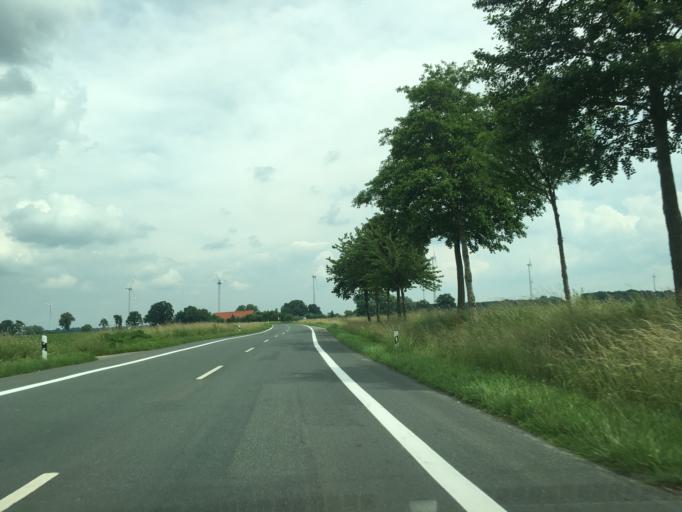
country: DE
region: North Rhine-Westphalia
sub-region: Regierungsbezirk Munster
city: Laer
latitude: 52.0717
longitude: 7.3936
